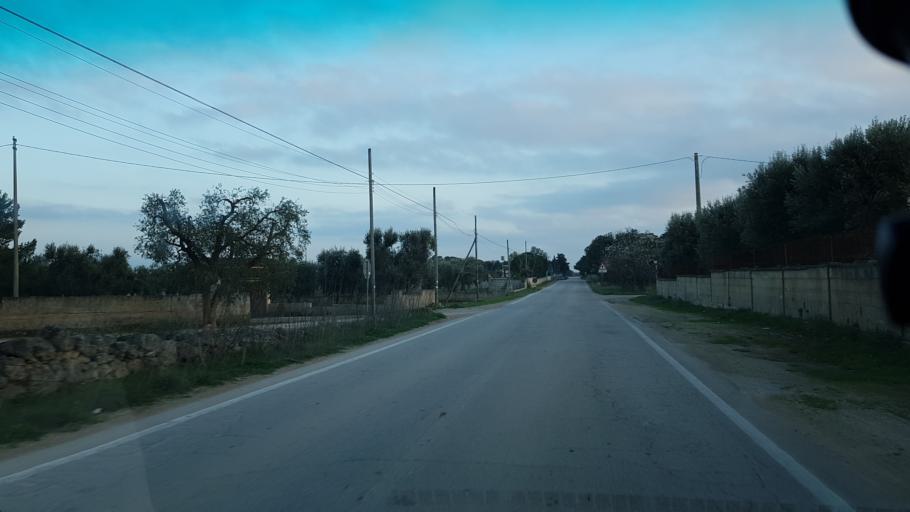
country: IT
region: Apulia
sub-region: Provincia di Brindisi
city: San Vito dei Normanni
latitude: 40.6457
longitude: 17.7767
